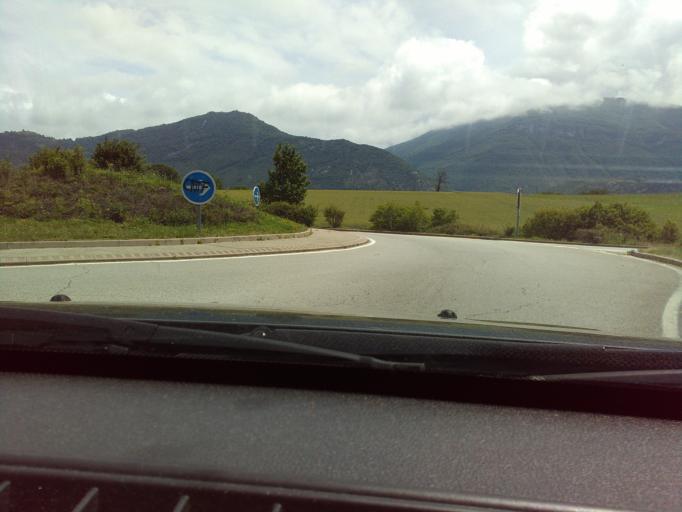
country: FR
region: Rhone-Alpes
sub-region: Departement de la Savoie
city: Saint-Baldoph
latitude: 45.5374
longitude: 5.9680
